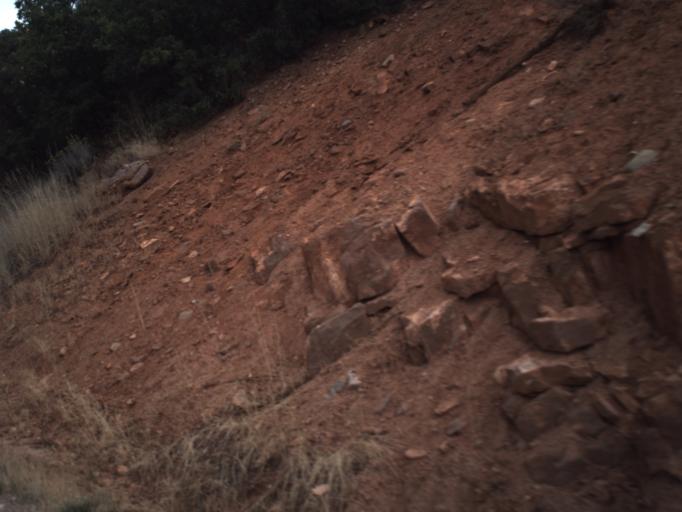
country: US
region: Utah
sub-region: Morgan County
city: Morgan
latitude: 40.9432
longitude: -111.6466
